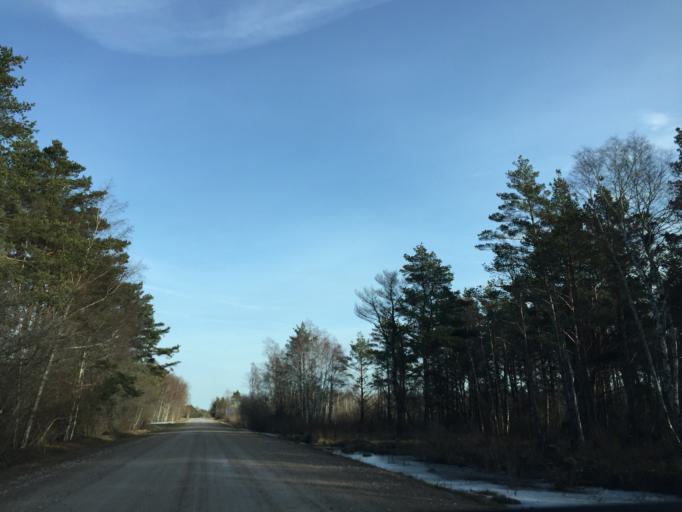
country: EE
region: Saare
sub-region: Kuressaare linn
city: Kuressaare
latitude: 58.3190
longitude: 21.9951
